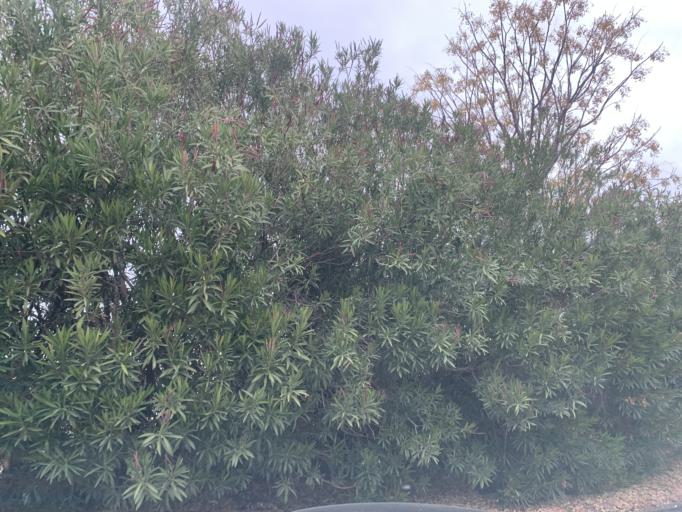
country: US
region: Arizona
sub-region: Pinal County
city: Arizona City
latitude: 32.8153
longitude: -111.6726
